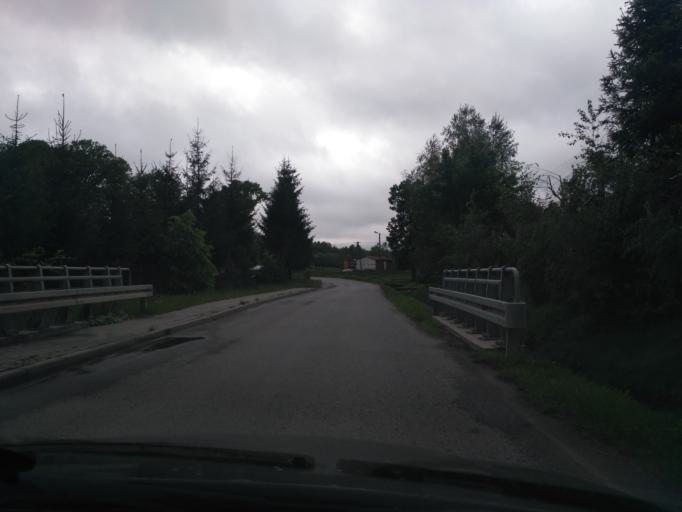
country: PL
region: Subcarpathian Voivodeship
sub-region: Powiat strzyzowski
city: Frysztak
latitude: 49.8048
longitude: 21.5824
